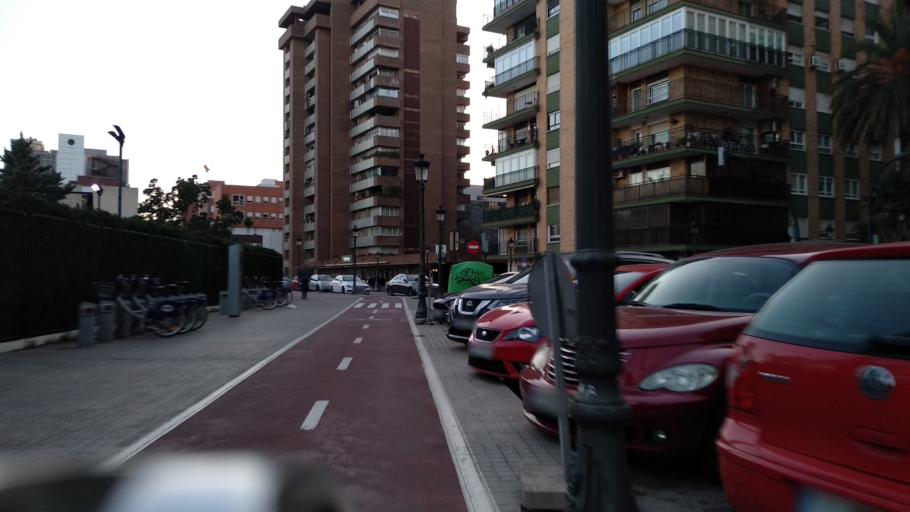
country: ES
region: Valencia
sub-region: Provincia de Valencia
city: Tavernes Blanques
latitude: 39.4811
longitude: -0.3608
